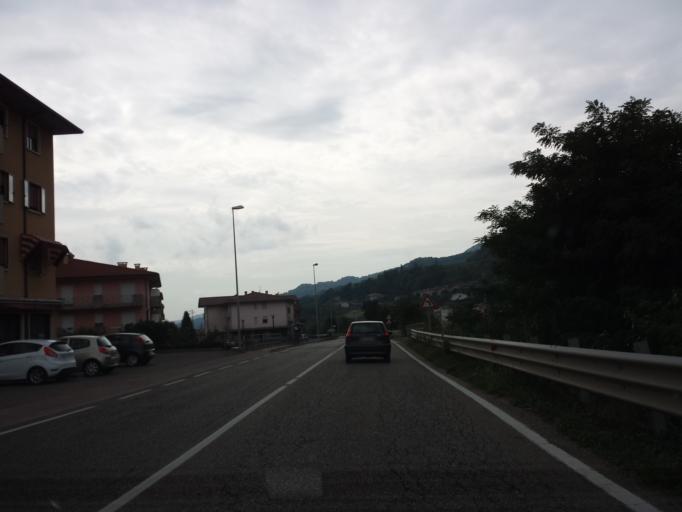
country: IT
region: Veneto
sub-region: Provincia di Verona
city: San Giovanni Ilarione
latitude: 45.5234
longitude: 11.2338
